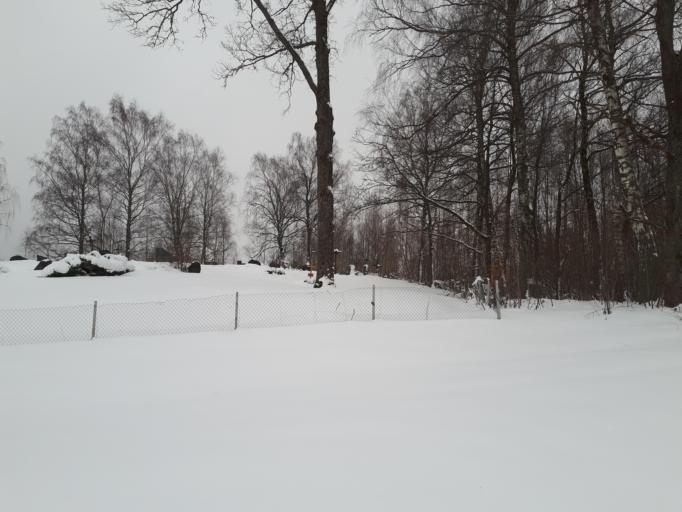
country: LT
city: Jieznas
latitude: 54.4683
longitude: 24.2089
